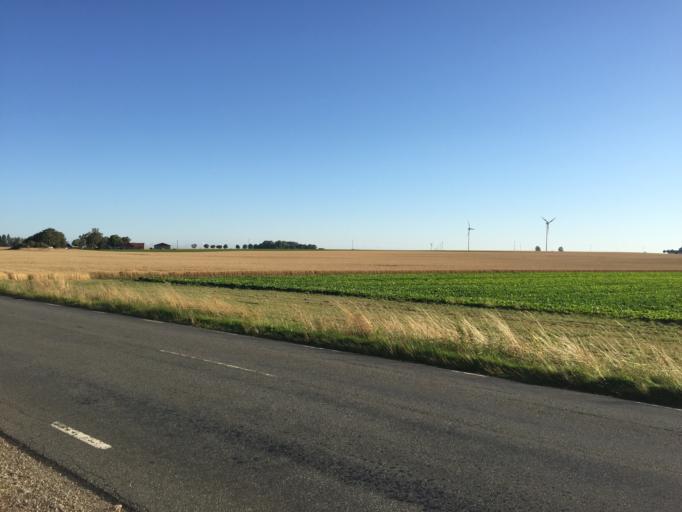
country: SE
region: Skane
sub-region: Ystads Kommun
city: Kopingebro
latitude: 55.4535
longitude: 14.1144
